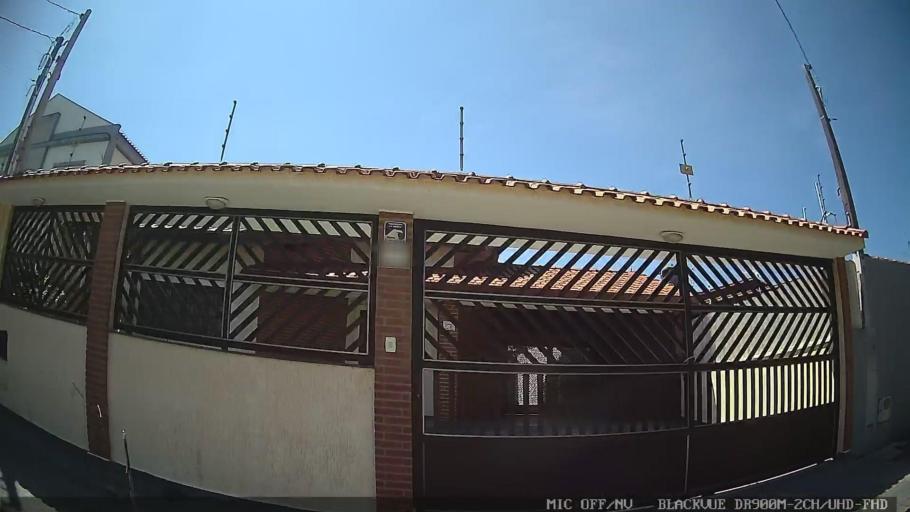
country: BR
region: Sao Paulo
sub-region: Peruibe
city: Peruibe
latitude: -24.3022
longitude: -46.9721
